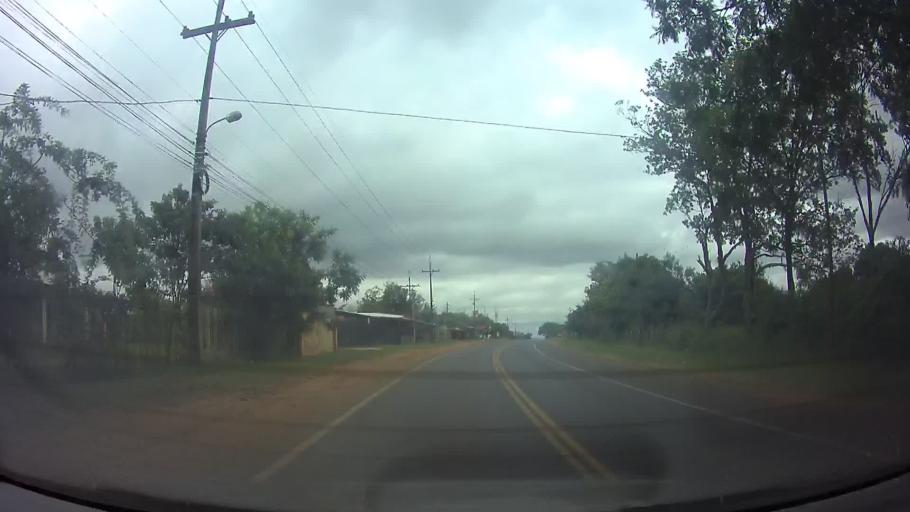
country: PY
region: Central
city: Guarambare
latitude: -25.5016
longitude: -57.4956
